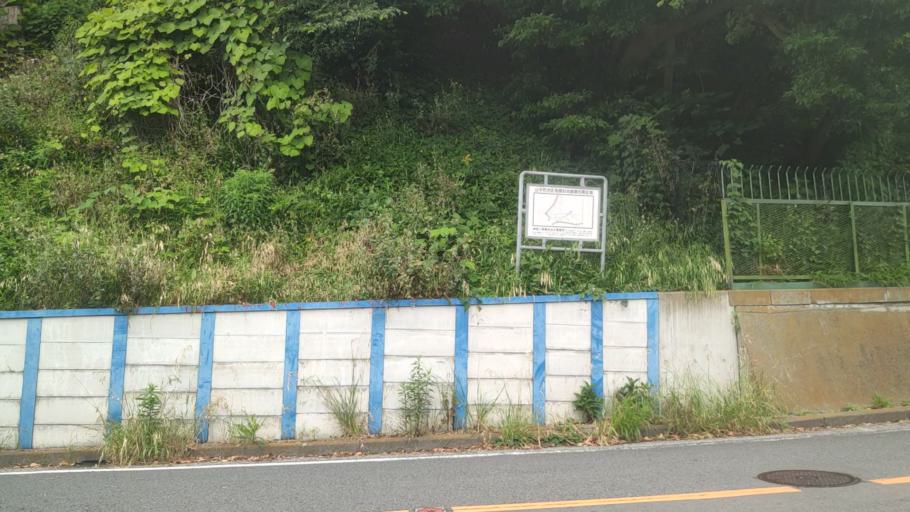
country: JP
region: Kanagawa
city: Yokohama
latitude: 35.4350
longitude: 139.6529
